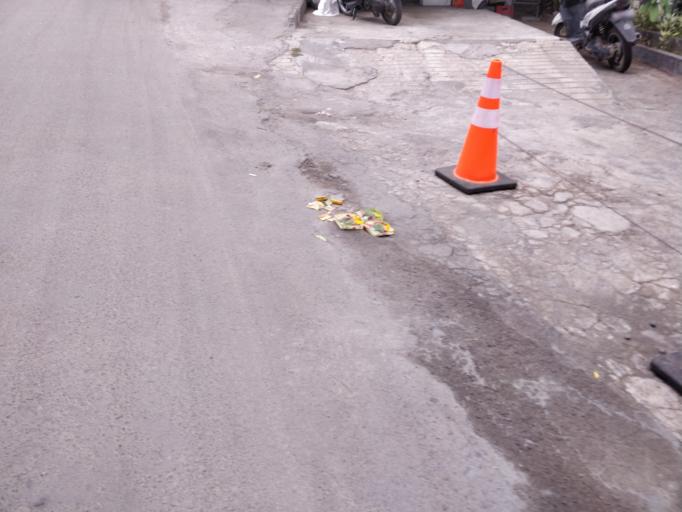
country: ID
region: Bali
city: Lembongan Kawan
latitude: -8.6840
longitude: 115.4346
